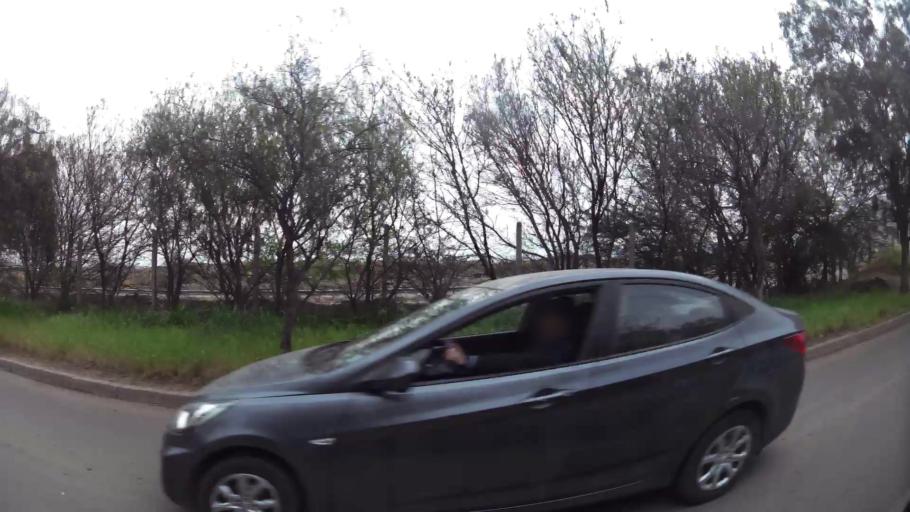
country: CL
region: Santiago Metropolitan
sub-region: Provincia de Chacabuco
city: Chicureo Abajo
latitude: -33.2003
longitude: -70.6611
